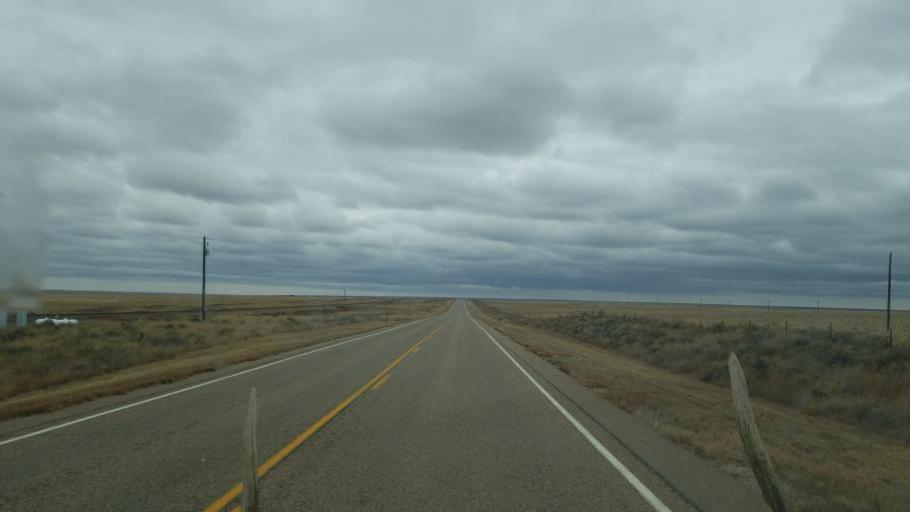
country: US
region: Colorado
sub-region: Kiowa County
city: Eads
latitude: 38.7741
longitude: -102.7487
